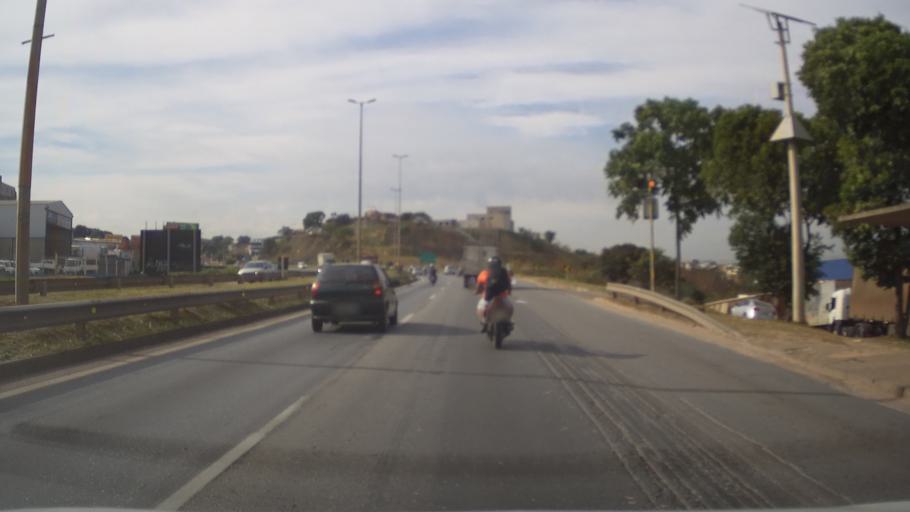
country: BR
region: Minas Gerais
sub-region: Contagem
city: Contagem
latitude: -19.9178
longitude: -44.0394
